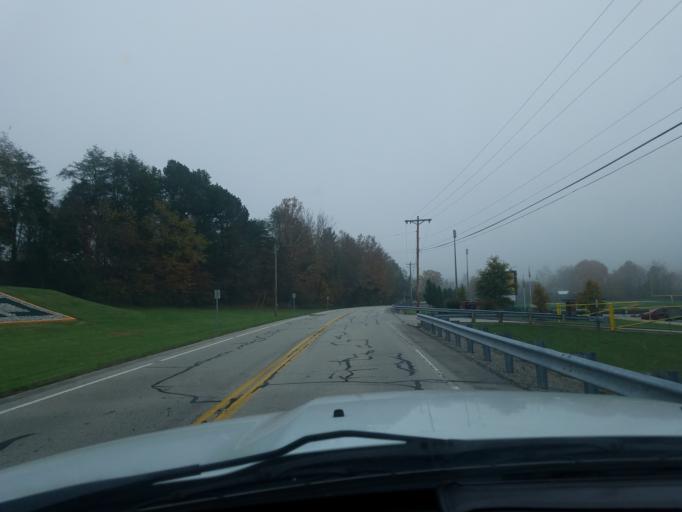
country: US
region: Indiana
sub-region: Floyd County
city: Galena
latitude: 38.3337
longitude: -85.9340
